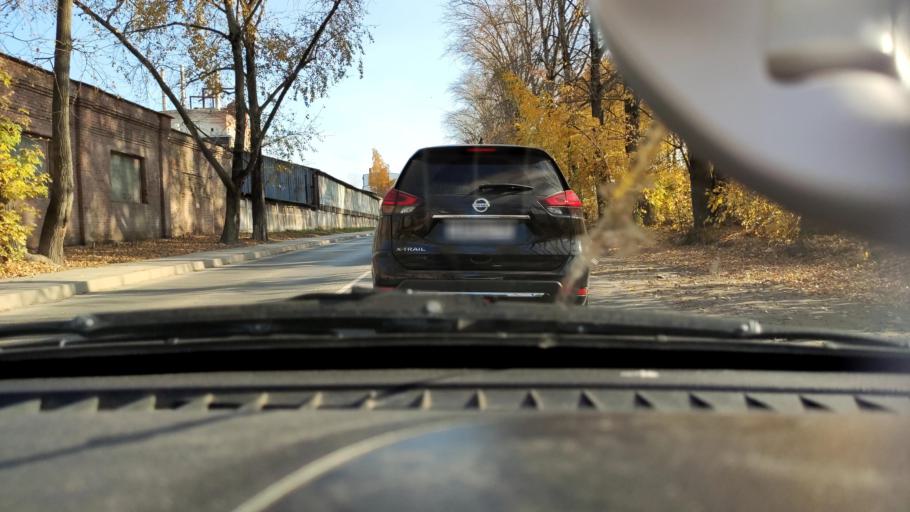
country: RU
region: Perm
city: Perm
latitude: 57.9596
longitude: 56.2077
